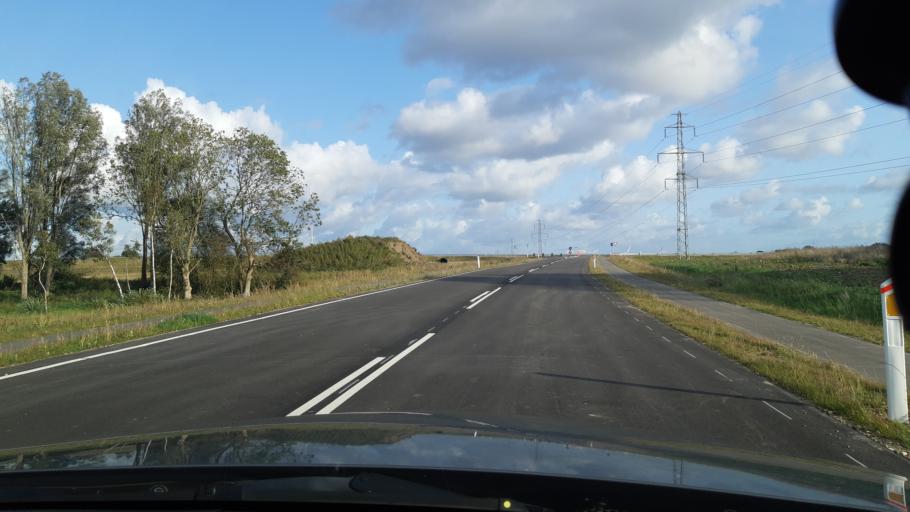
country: DK
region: Zealand
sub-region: Holbaek Kommune
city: Holbaek
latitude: 55.6595
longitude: 11.6128
